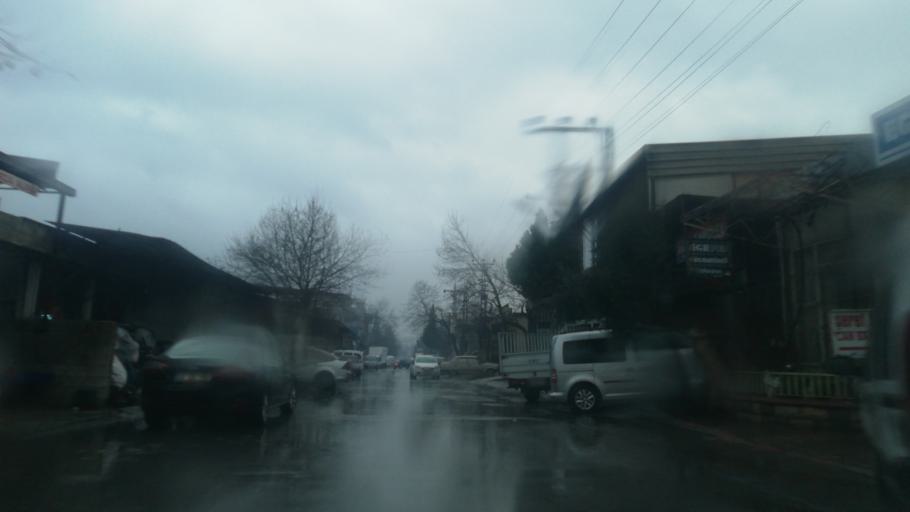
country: TR
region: Kahramanmaras
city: Kahramanmaras
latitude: 37.5606
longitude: 36.9603
